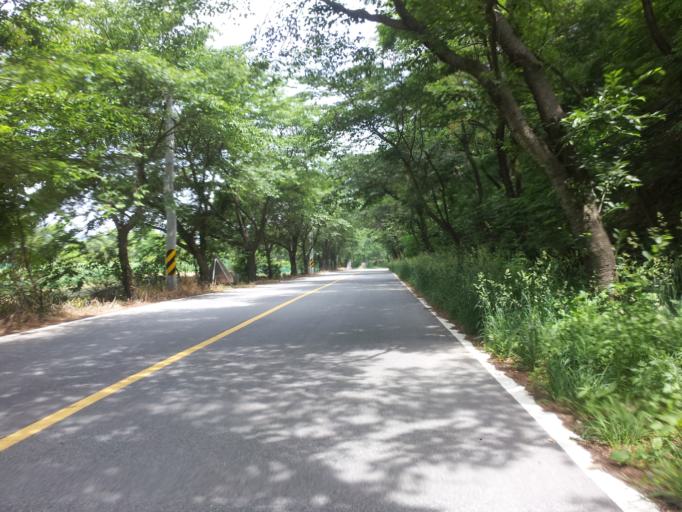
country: KR
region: Chungcheongbuk-do
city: Okcheon
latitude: 36.3830
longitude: 127.5187
